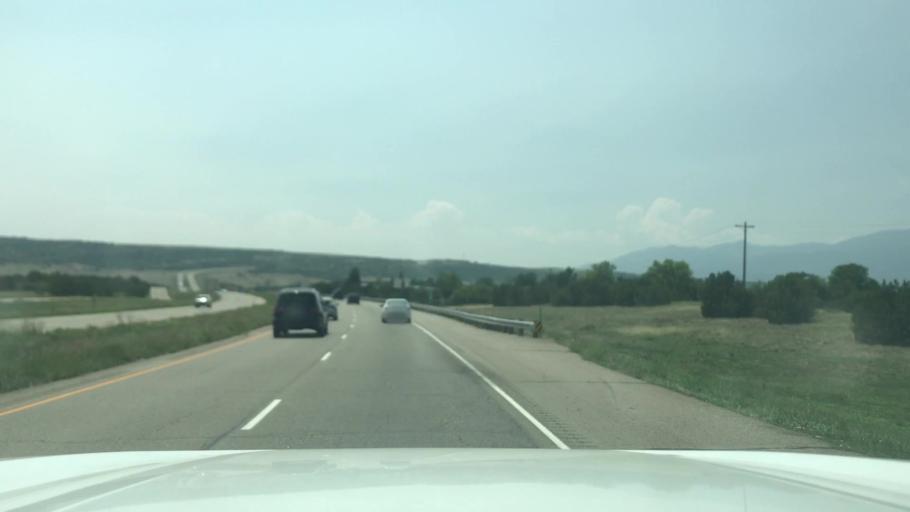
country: US
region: Colorado
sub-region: Pueblo County
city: Colorado City
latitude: 37.9587
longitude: -104.7990
